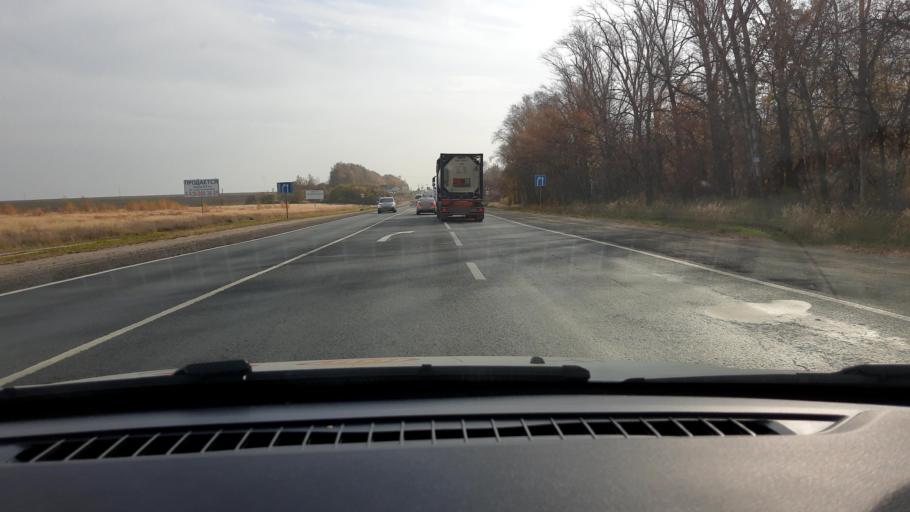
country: RU
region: Nizjnij Novgorod
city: Kstovo
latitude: 56.1211
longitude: 44.2720
